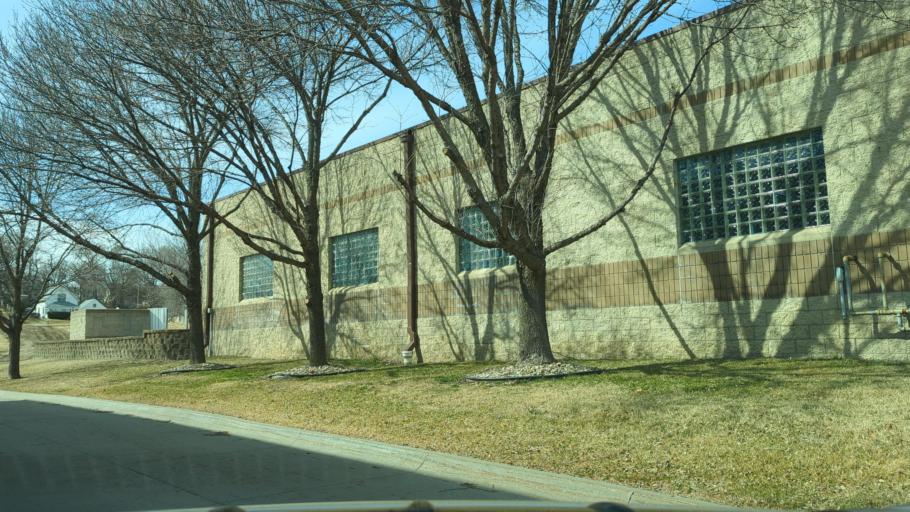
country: US
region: Nebraska
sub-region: Douglas County
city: Omaha
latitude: 41.2317
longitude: -95.9337
